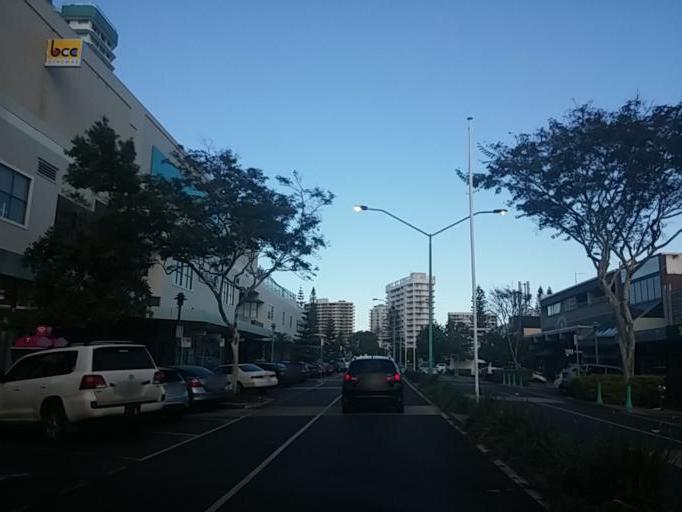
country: AU
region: New South Wales
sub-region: Tweed
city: Tweed Heads West
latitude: -28.1684
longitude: 153.5376
